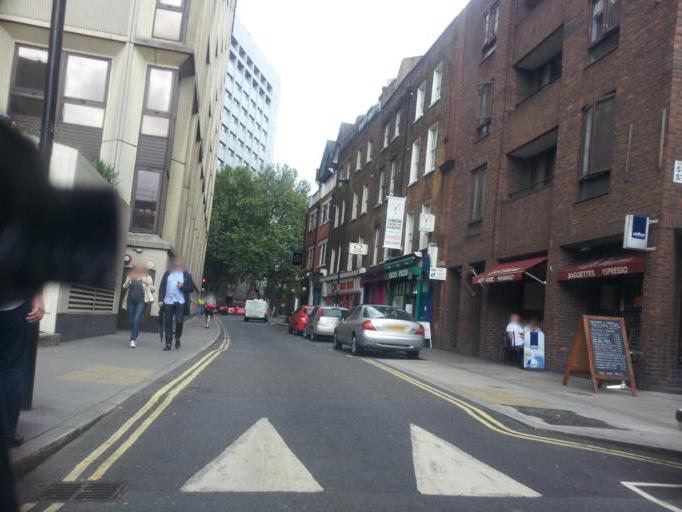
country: GB
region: England
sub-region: Greater London
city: London
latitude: 51.5158
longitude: -0.1238
